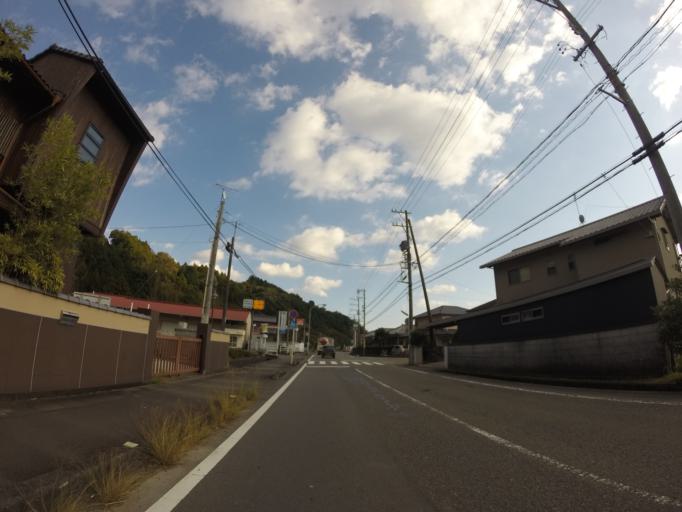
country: JP
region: Shizuoka
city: Kanaya
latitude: 34.8659
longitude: 138.1247
